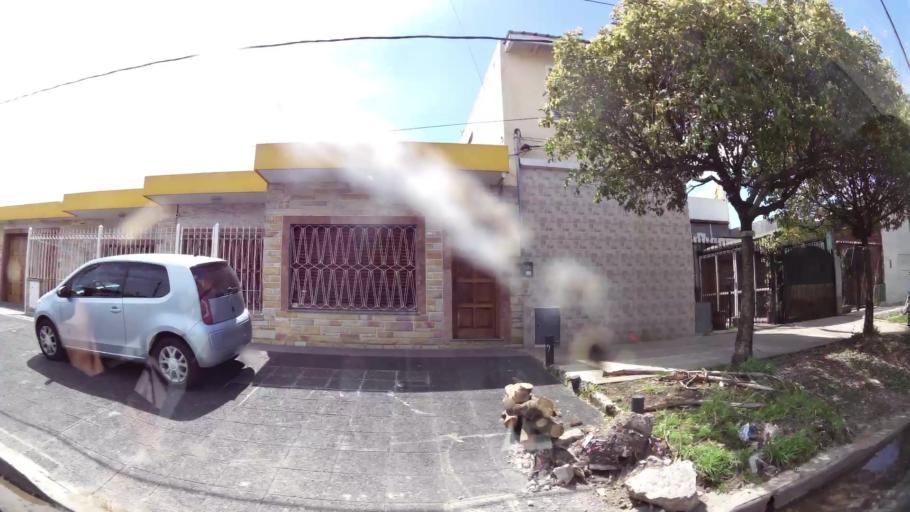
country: AR
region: Buenos Aires
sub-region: Partido de Quilmes
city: Quilmes
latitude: -34.7561
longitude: -58.2981
